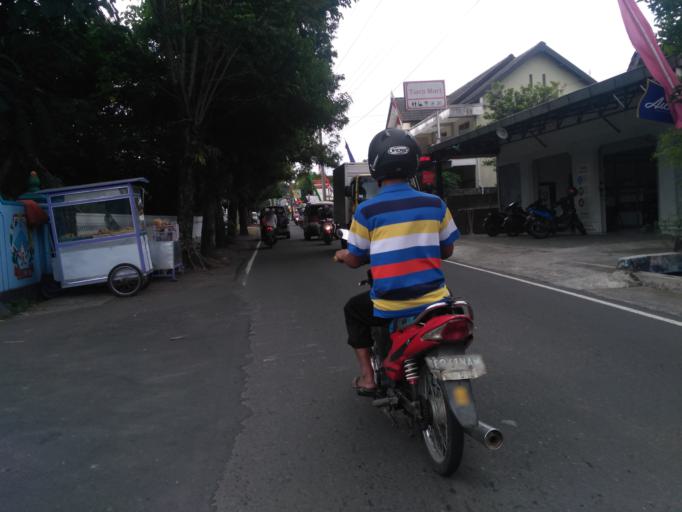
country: ID
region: Daerah Istimewa Yogyakarta
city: Sleman
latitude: -7.7261
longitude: 110.3568
